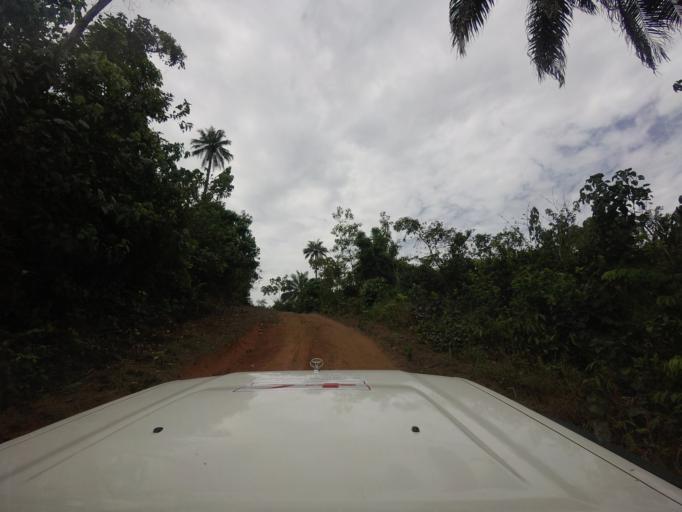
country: SL
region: Eastern Province
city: Buedu
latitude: 8.2290
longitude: -10.2638
